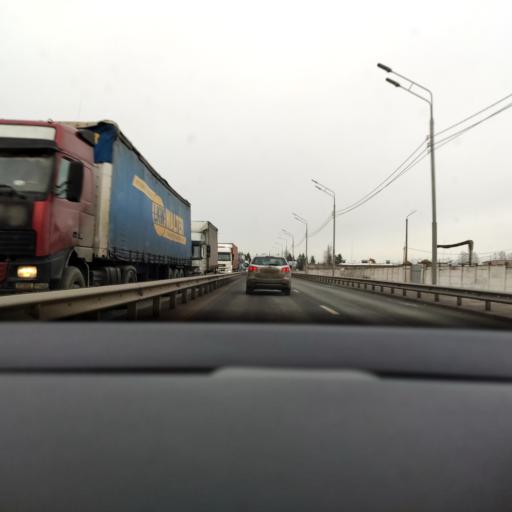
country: RU
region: Moskovskaya
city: Bol'shiye Vyazemy
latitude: 55.6328
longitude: 37.0047
